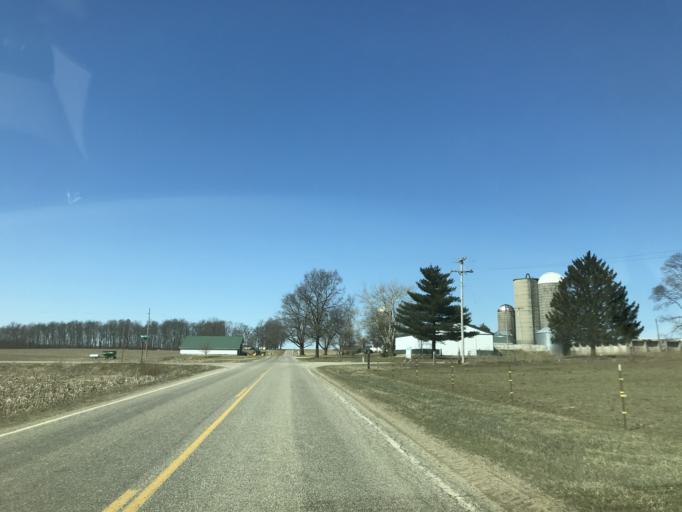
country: US
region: Michigan
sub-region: Hillsdale County
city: Jonesville
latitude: 41.9855
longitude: -84.6891
